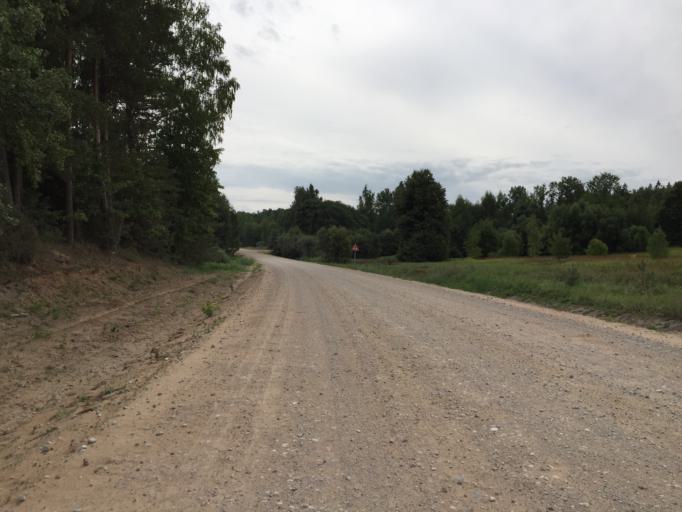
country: LV
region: Jaunpils
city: Jaunpils
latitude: 56.7255
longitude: 23.1444
